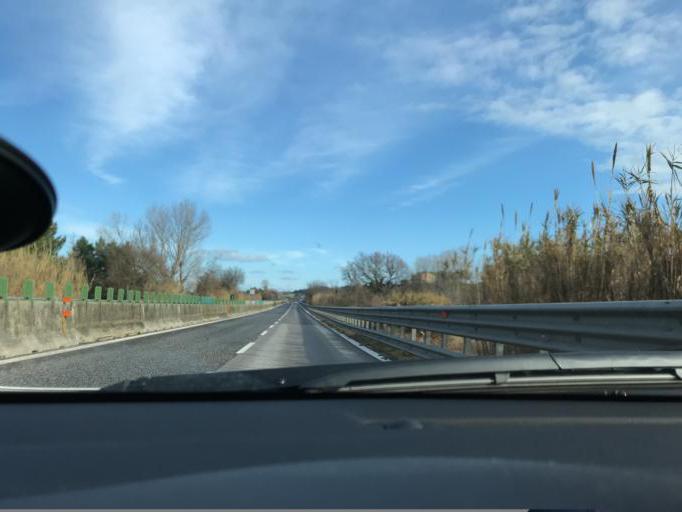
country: IT
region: The Marches
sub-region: Provincia di Ancona
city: Falconara Marittima
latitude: 43.6076
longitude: 13.3723
